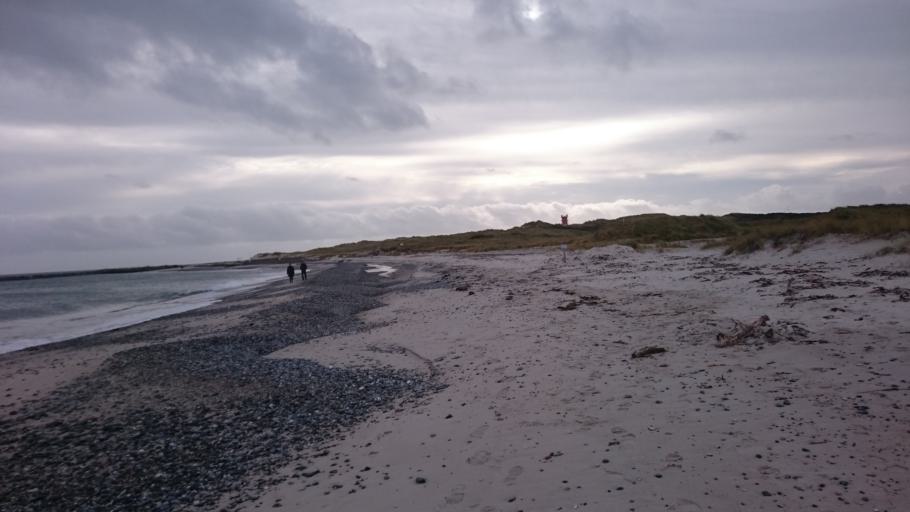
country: DE
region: Schleswig-Holstein
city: Helgoland
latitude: 54.1856
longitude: 7.9174
